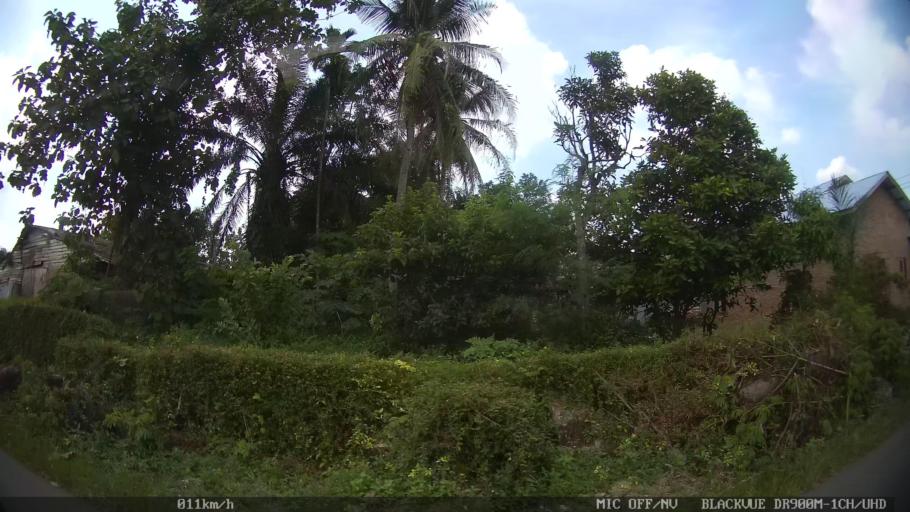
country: ID
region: North Sumatra
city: Binjai
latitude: 3.6354
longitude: 98.5172
